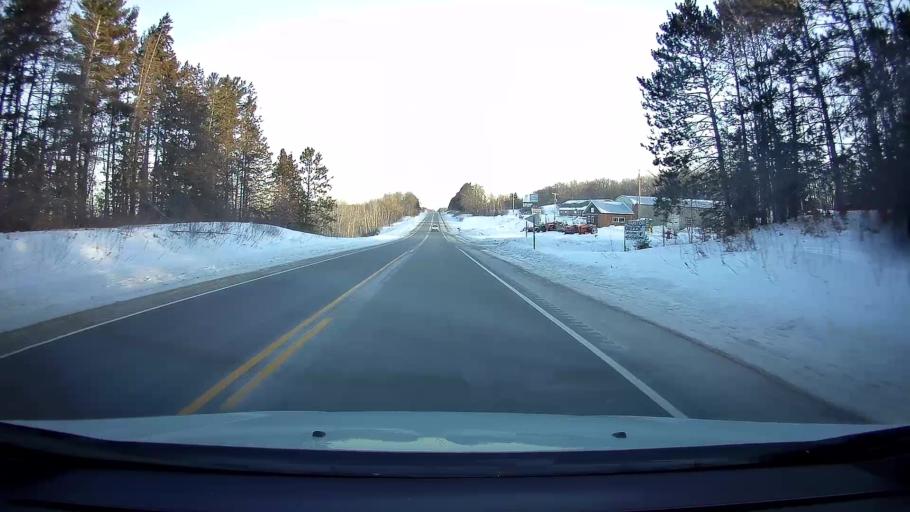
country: US
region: Wisconsin
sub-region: Washburn County
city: Shell Lake
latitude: 45.7567
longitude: -91.9149
